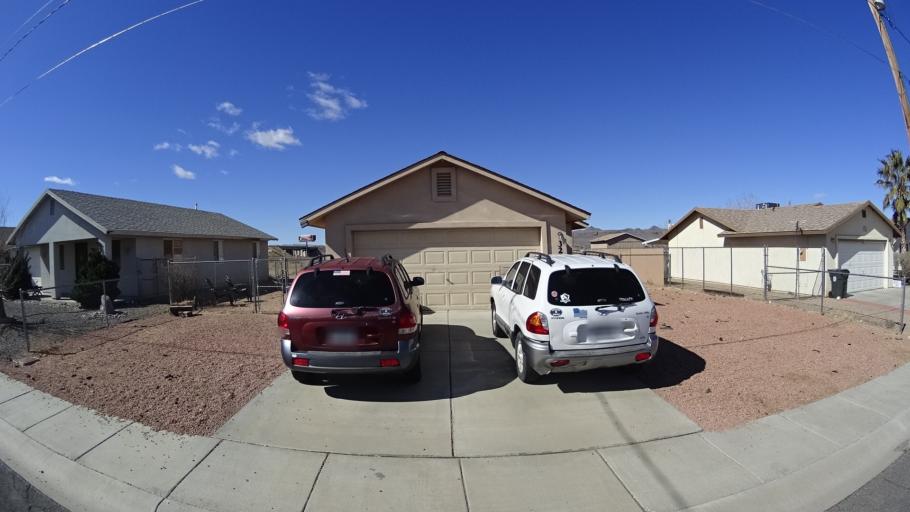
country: US
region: Arizona
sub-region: Mohave County
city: New Kingman-Butler
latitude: 35.2188
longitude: -114.0027
